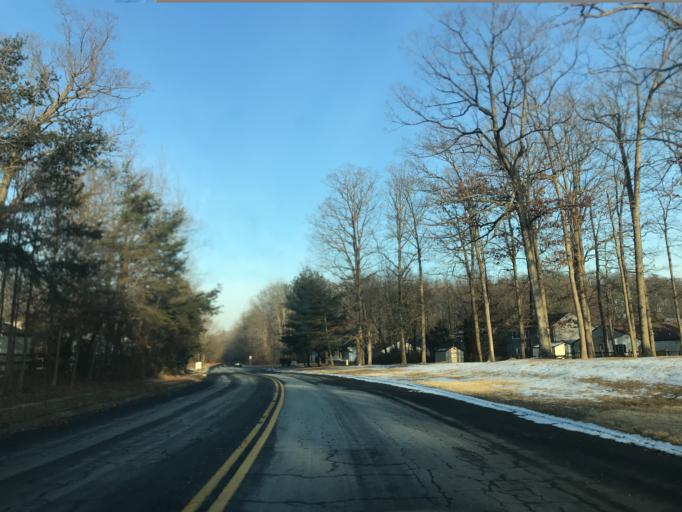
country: US
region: Maryland
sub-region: Harford County
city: Edgewood
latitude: 39.4308
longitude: -76.2666
